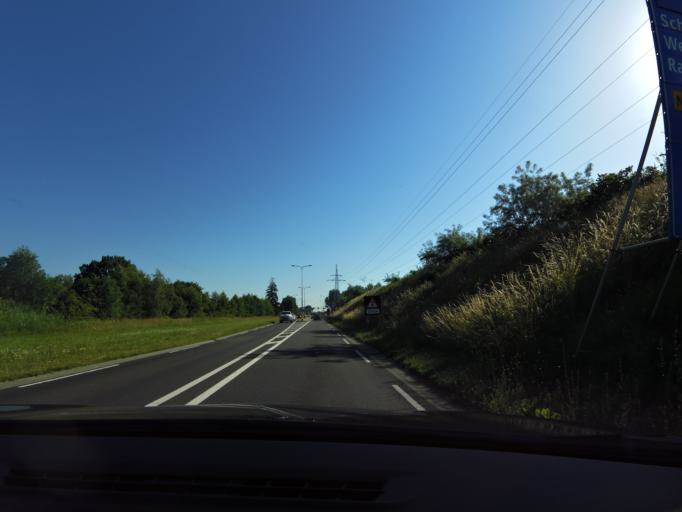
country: NL
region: Overijssel
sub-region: Gemeente Deventer
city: Schalkhaar
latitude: 52.2648
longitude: 6.2115
